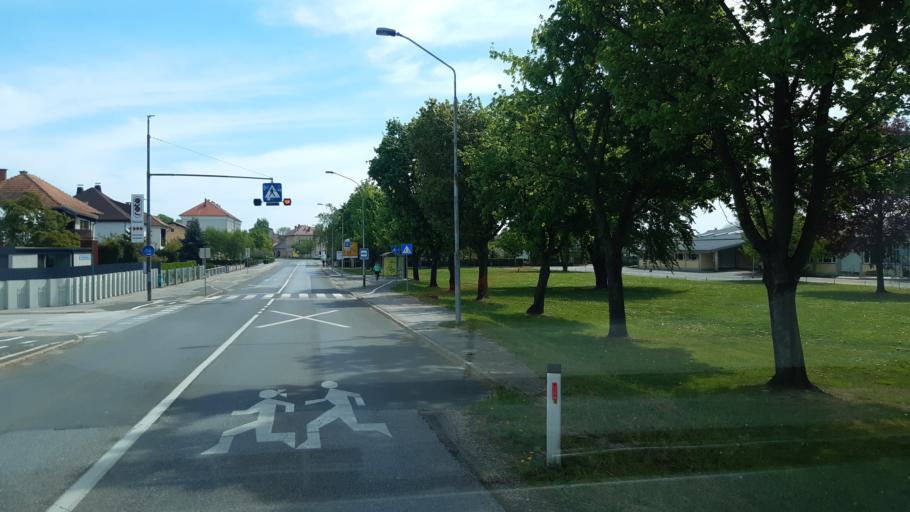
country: SI
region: Murska Sobota
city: Murska Sobota
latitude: 46.6615
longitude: 16.1511
